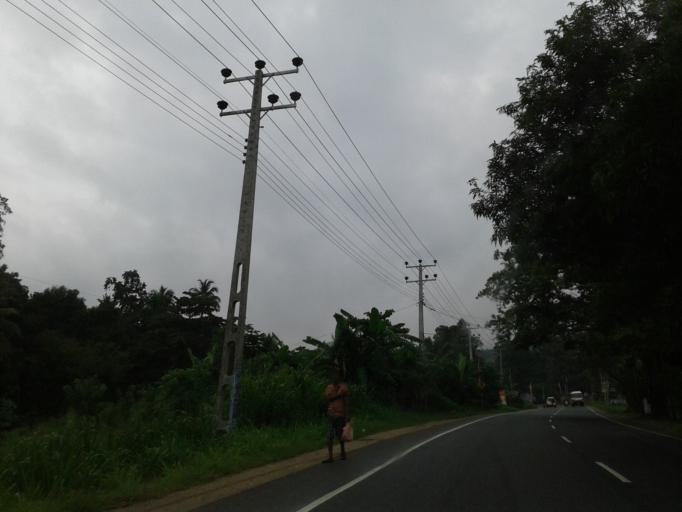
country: LK
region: Western
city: Gampaha
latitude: 7.2385
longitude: 80.2298
